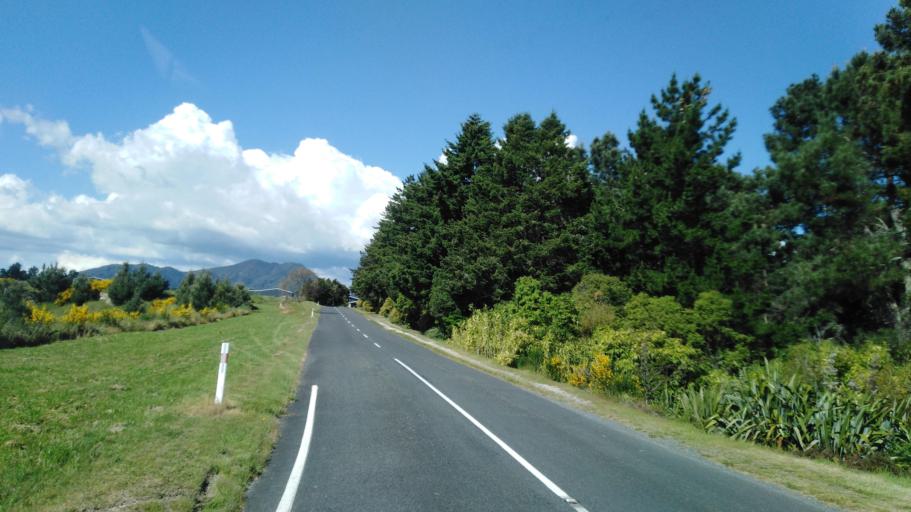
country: NZ
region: Waikato
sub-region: Taupo District
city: Taupo
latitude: -38.7397
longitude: 176.0772
